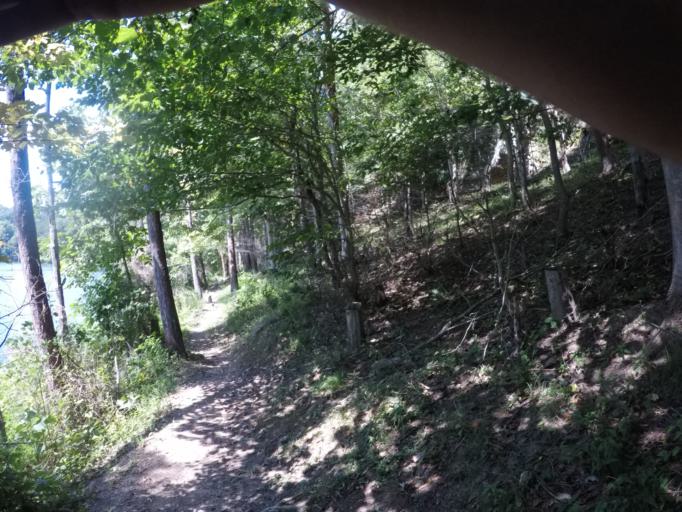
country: US
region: Ohio
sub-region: Lawrence County
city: Ironton
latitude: 38.6089
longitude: -82.6282
